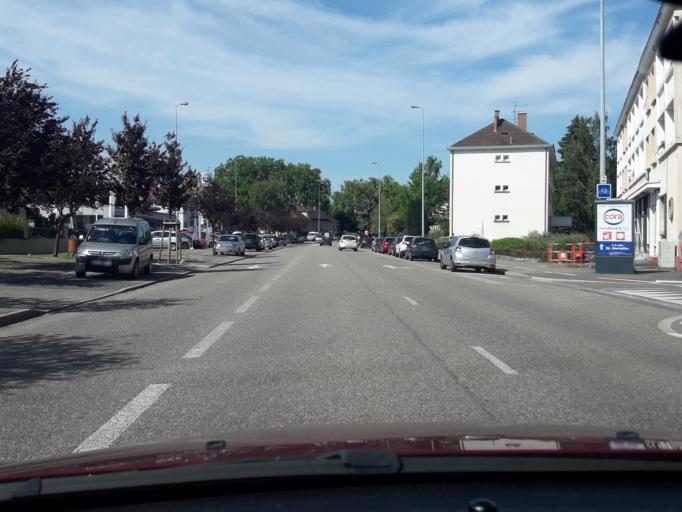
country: FR
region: Alsace
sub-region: Departement du Bas-Rhin
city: Haguenau
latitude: 48.8155
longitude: 7.7833
